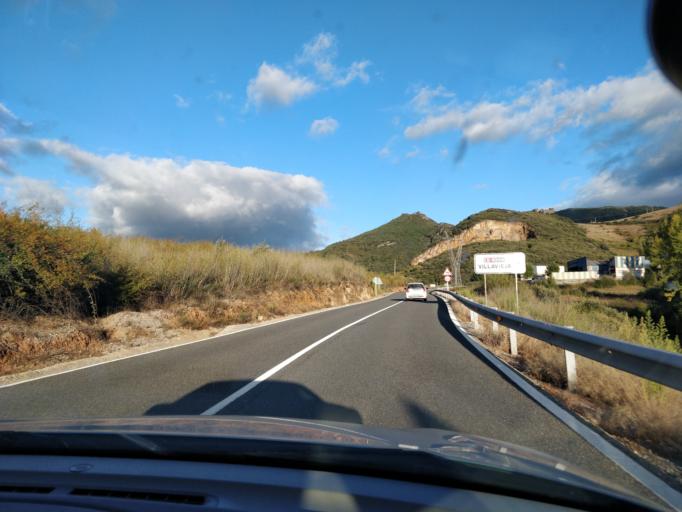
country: ES
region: Castille and Leon
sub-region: Provincia de Leon
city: Borrenes
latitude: 42.4919
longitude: -6.7049
